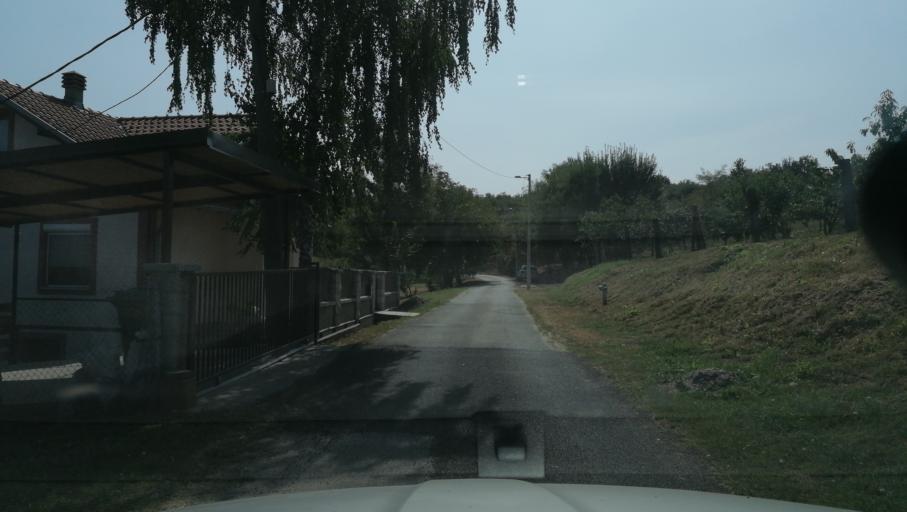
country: RS
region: Central Serbia
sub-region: Belgrade
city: Zvezdara
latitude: 44.6928
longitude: 20.5568
